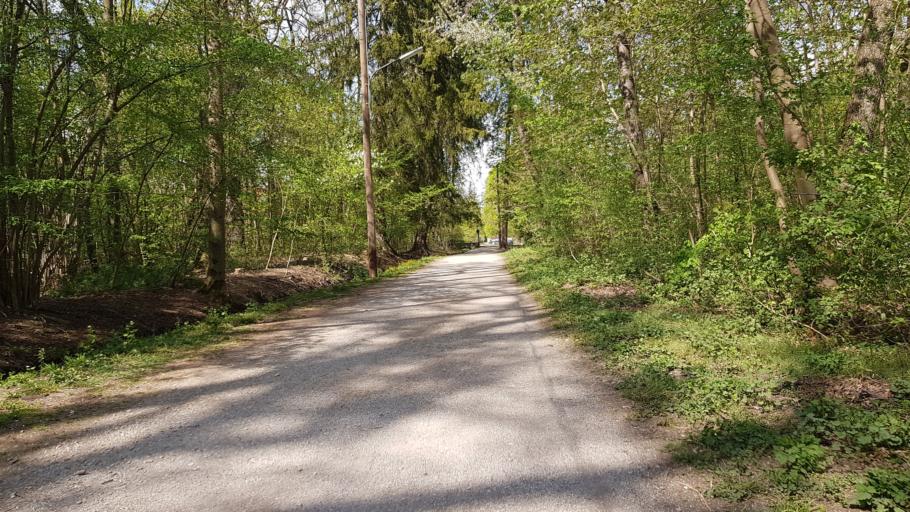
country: DE
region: Bavaria
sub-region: Upper Bavaria
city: Karlsfeld
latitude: 48.1744
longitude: 11.4944
